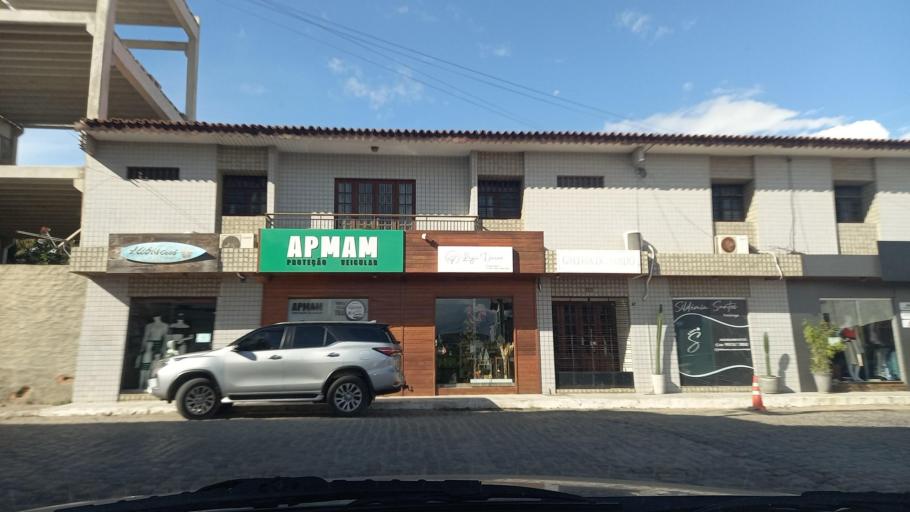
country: BR
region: Pernambuco
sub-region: Gravata
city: Gravata
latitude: -8.2004
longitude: -35.5633
